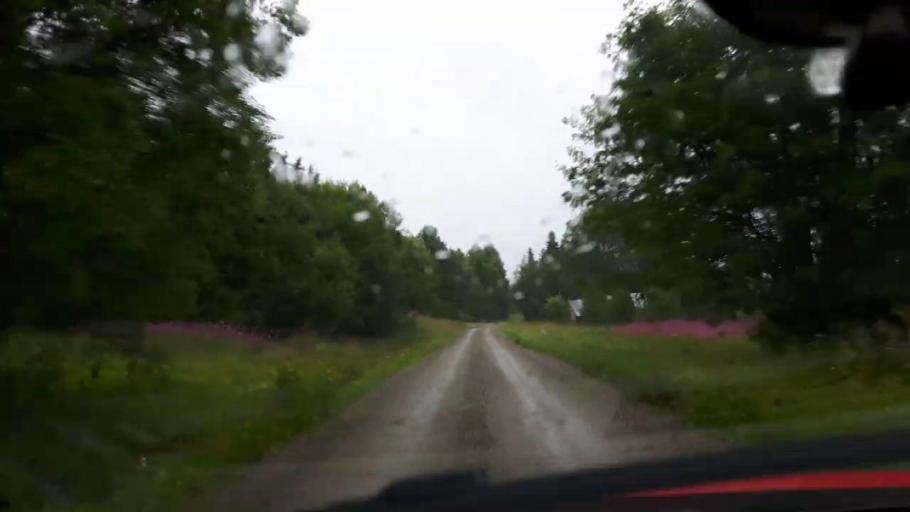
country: SE
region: Jaemtland
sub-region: OEstersunds Kommun
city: Brunflo
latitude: 62.7875
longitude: 14.9653
